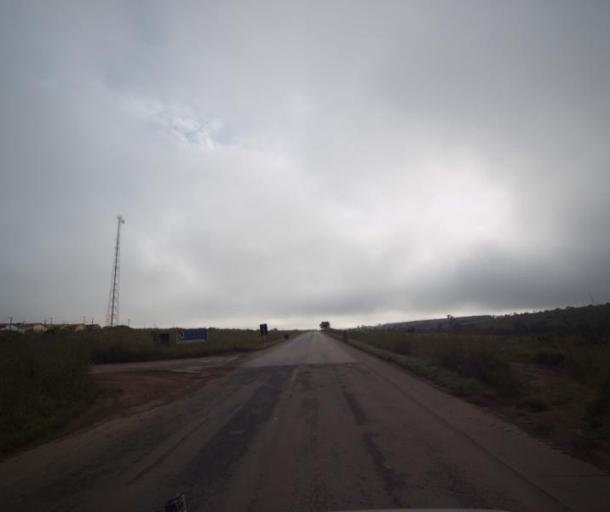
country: BR
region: Goias
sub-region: Pirenopolis
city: Pirenopolis
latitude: -15.7697
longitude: -48.7610
